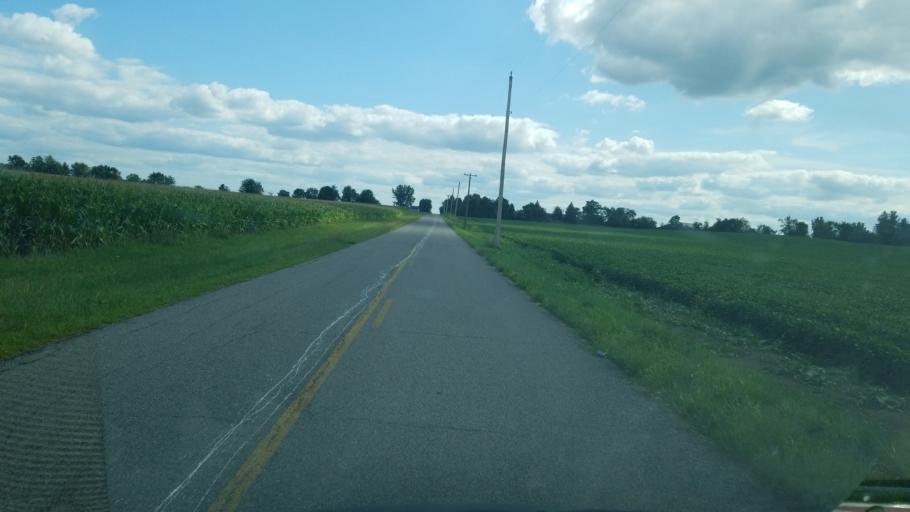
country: US
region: Ohio
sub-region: Logan County
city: Lakeview
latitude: 40.5420
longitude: -83.9749
